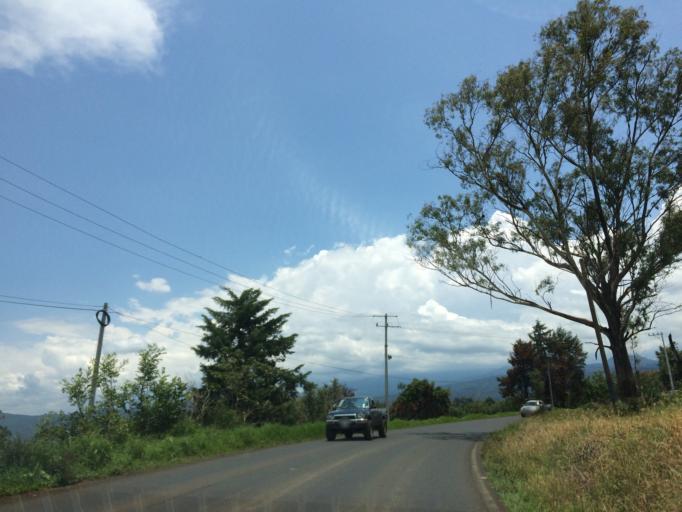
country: MX
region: Michoacan
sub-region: Periban
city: San Francisco Periban
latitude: 19.5413
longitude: -102.4122
